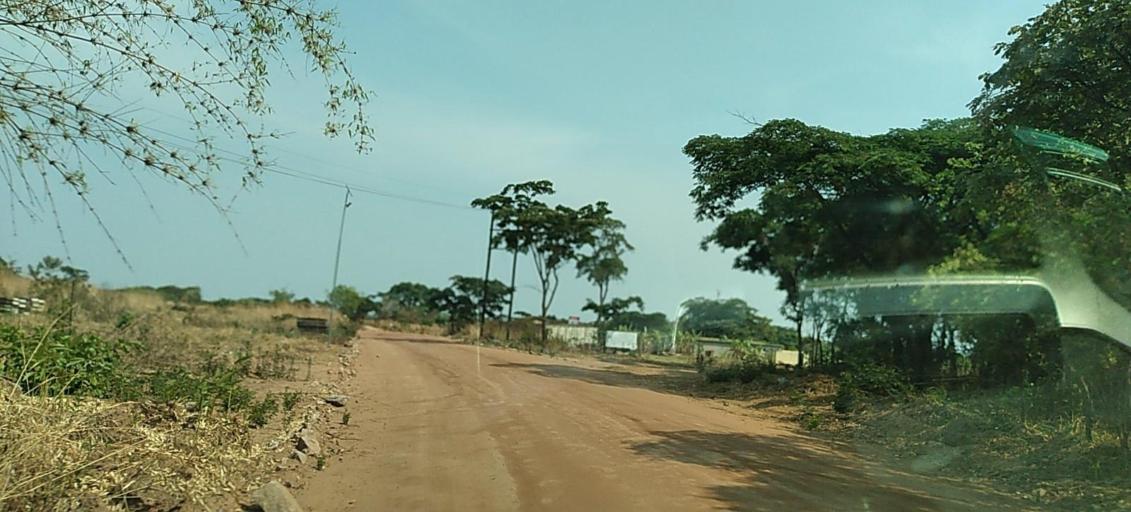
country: ZM
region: Copperbelt
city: Chililabombwe
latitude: -12.2940
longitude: 27.7692
